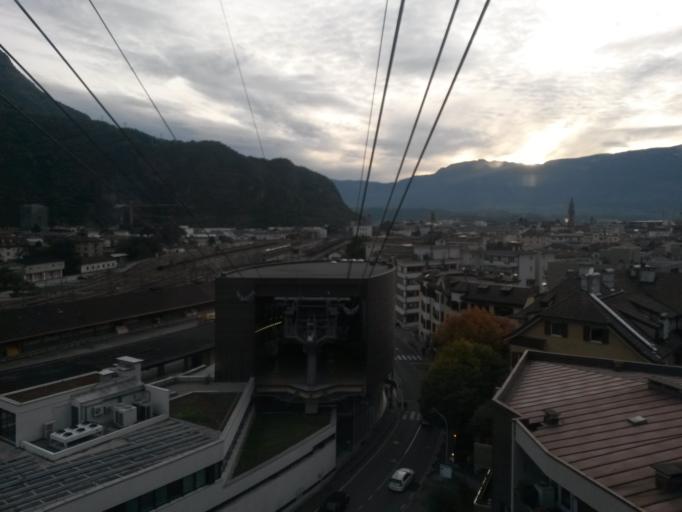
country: IT
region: Trentino-Alto Adige
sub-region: Bolzano
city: Bolzano
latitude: 46.5004
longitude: 11.3648
